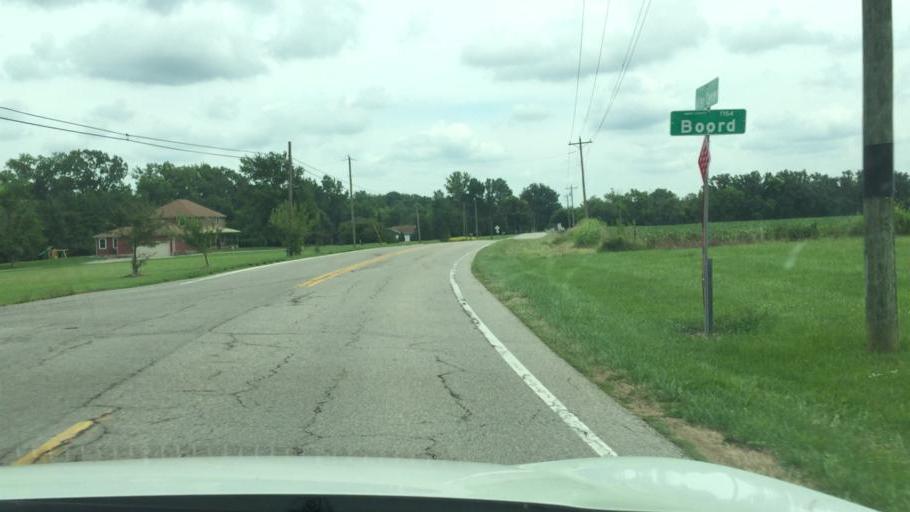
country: US
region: Ohio
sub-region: Champaign County
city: North Lewisburg
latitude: 40.2333
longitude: -83.4649
